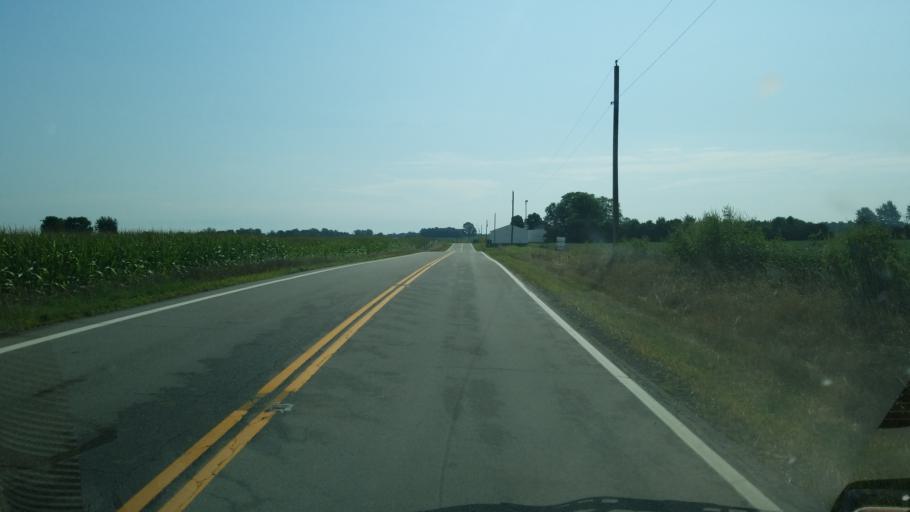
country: US
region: Ohio
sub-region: Richland County
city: Shelby
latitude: 40.8468
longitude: -82.7037
